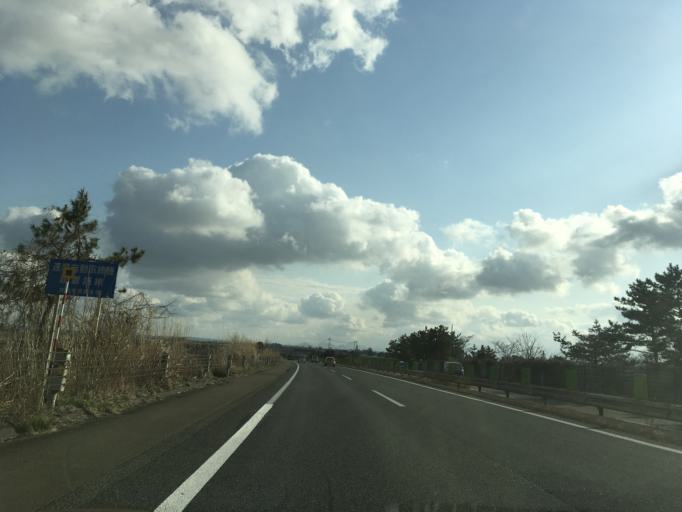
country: JP
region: Miyagi
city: Furukawa
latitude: 38.6253
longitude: 140.9479
